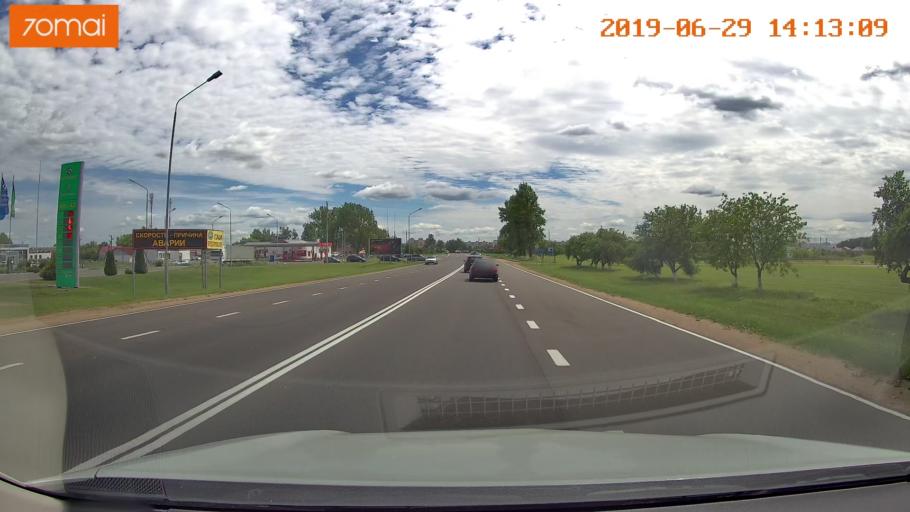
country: BY
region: Minsk
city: Salihorsk
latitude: 52.8046
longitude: 27.5099
